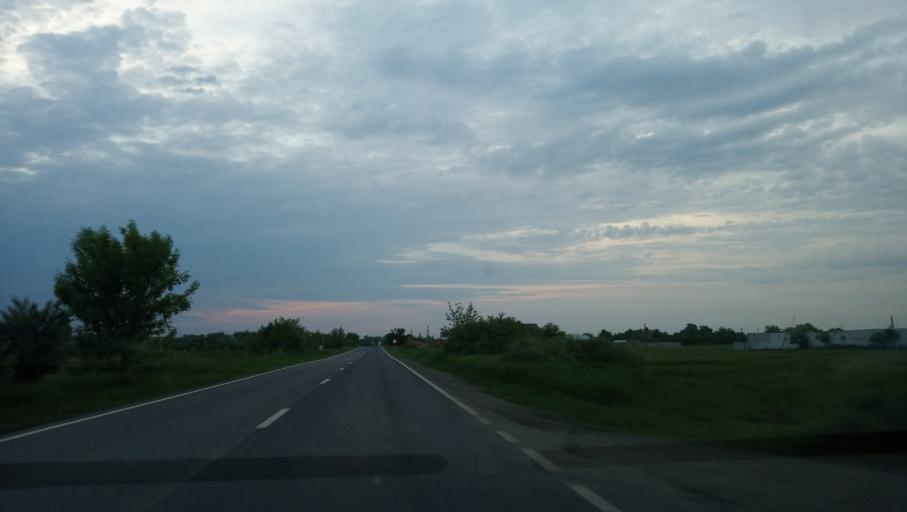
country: RO
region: Timis
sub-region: Comuna Jebel
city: Jebel
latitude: 45.5482
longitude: 21.2236
